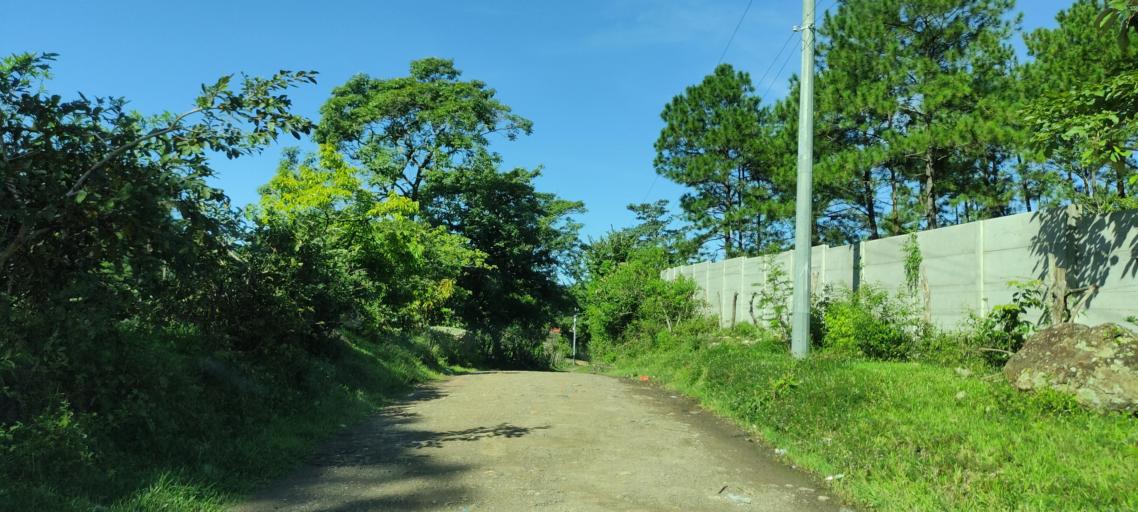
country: HN
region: Ocotepeque
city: Antigua Ocotepeque
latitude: 14.3172
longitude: -89.1790
